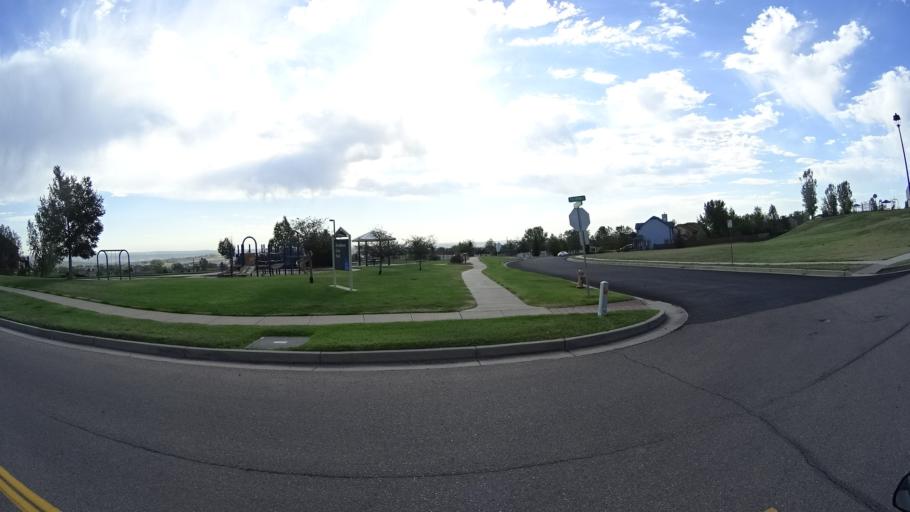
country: US
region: Colorado
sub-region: El Paso County
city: Fort Carson
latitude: 38.7587
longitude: -104.8143
